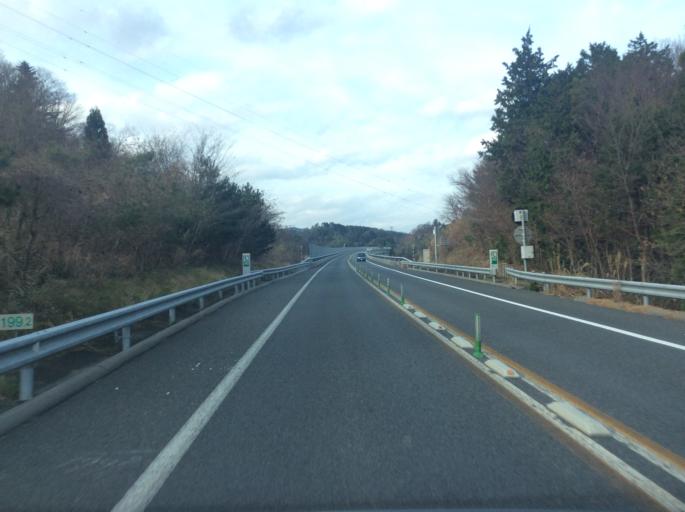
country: JP
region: Fukushima
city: Iwaki
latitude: 37.2132
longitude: 140.9797
